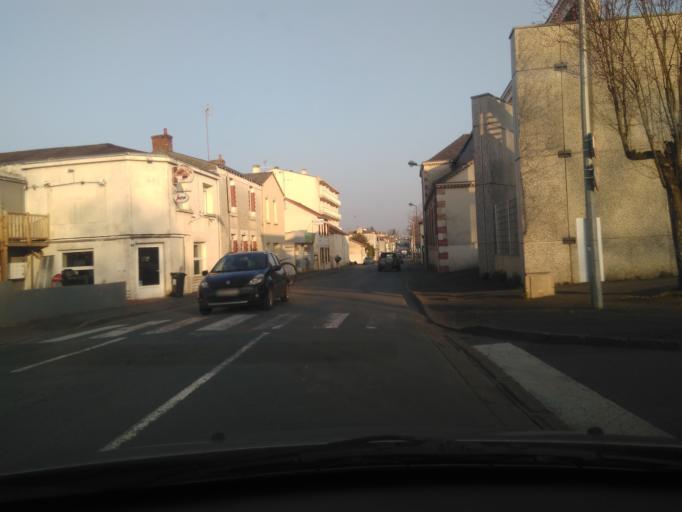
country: FR
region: Pays de la Loire
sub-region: Departement de la Vendee
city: Chantonnay
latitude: 46.6851
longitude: -1.0494
